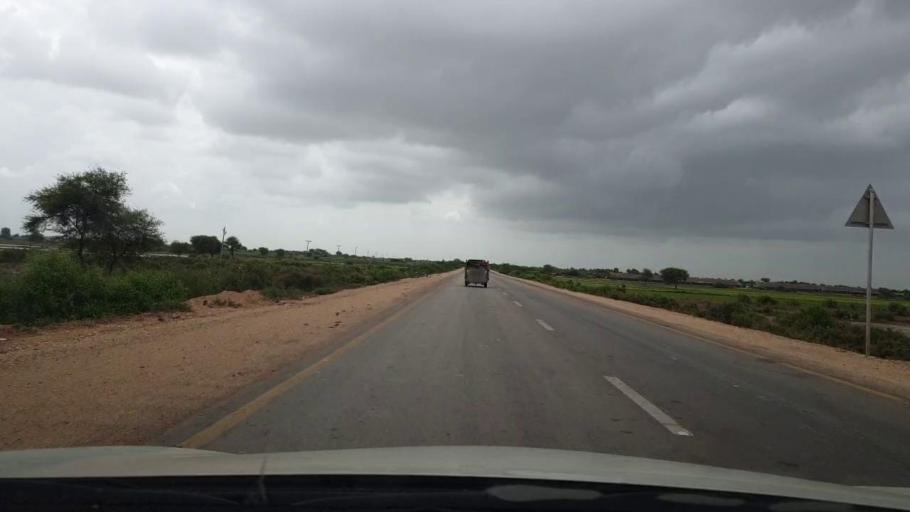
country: PK
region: Sindh
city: Mirpur Batoro
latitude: 24.6438
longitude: 68.4323
